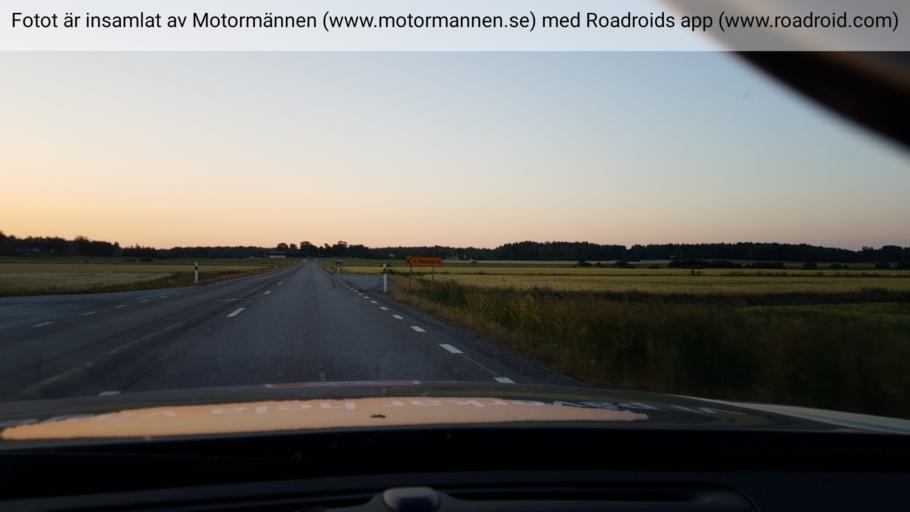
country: SE
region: Uppsala
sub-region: Heby Kommun
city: OEstervala
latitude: 60.0898
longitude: 17.1894
